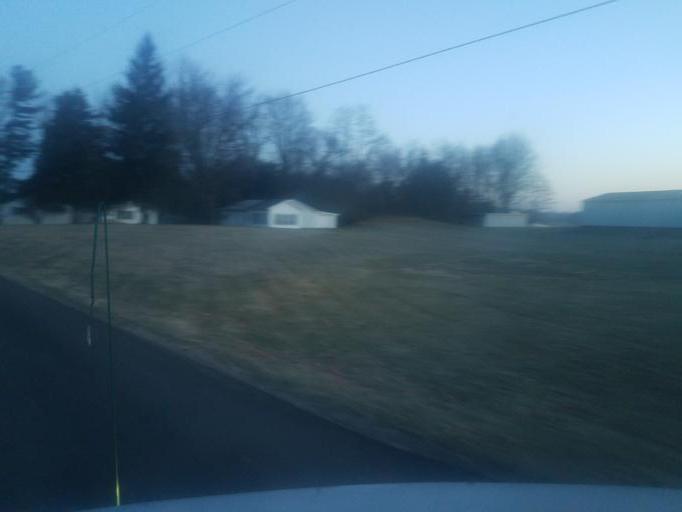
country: US
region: Ohio
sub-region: Crawford County
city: Galion
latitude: 40.6693
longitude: -82.8416
